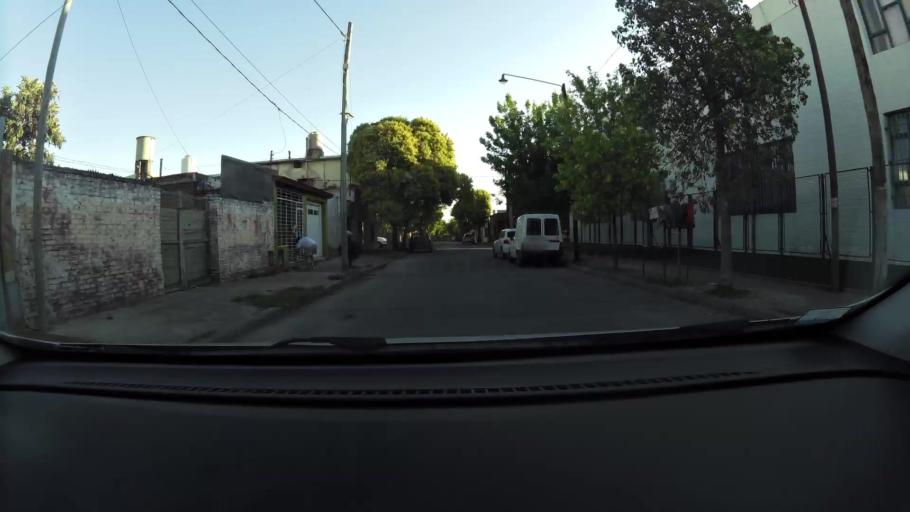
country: AR
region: Cordoba
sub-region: Departamento de Capital
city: Cordoba
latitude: -31.3746
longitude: -64.2079
